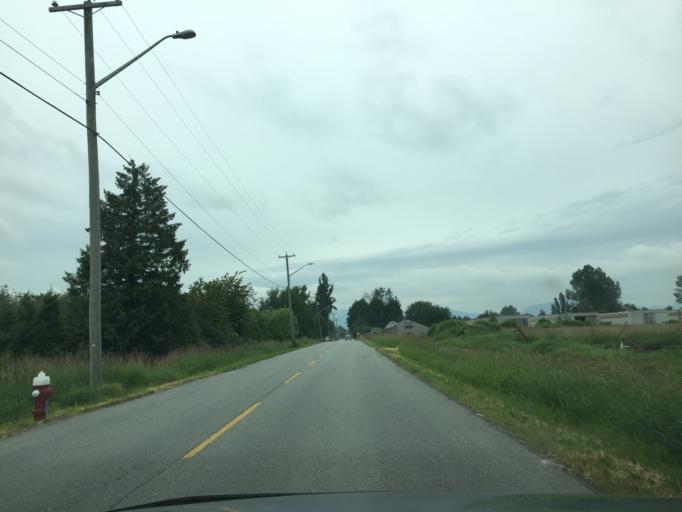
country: CA
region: British Columbia
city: Richmond
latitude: 49.1522
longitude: -123.0806
